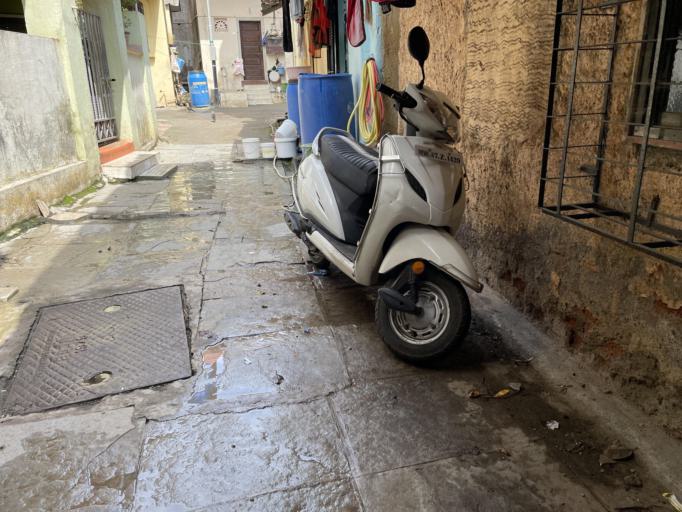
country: IN
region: Maharashtra
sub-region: Mumbai Suburban
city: Borivli
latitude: 19.2568
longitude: 72.8540
